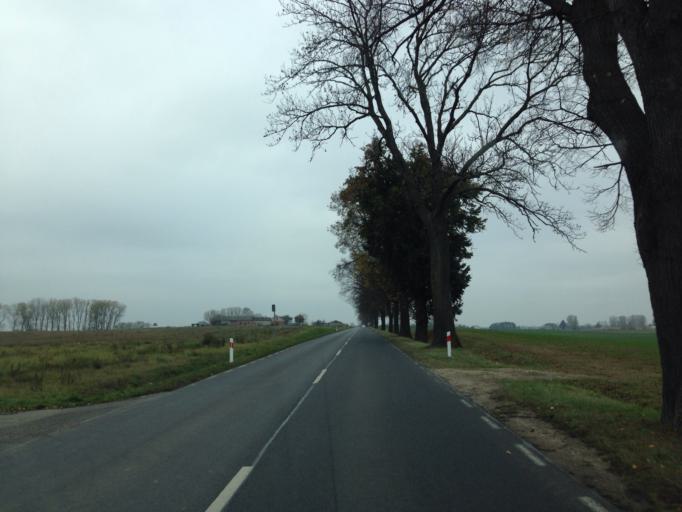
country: PL
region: Kujawsko-Pomorskie
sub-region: Powiat brodnicki
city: Jablonowo Pomorskie
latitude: 53.3858
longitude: 19.1281
